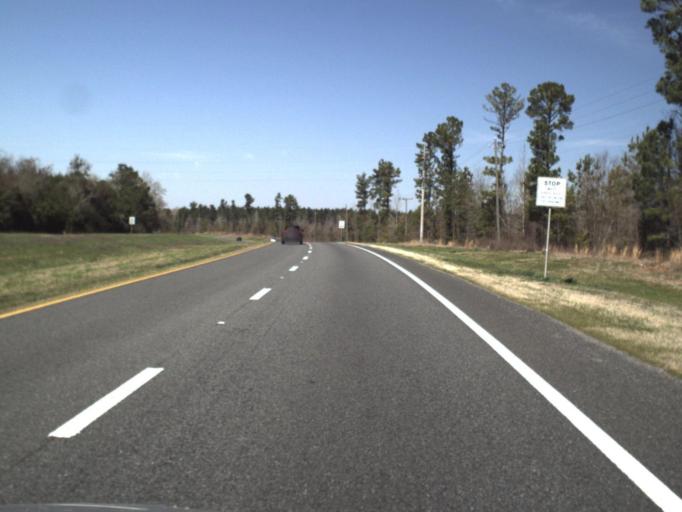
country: US
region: Florida
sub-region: Jackson County
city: Graceville
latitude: 30.9570
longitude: -85.4025
